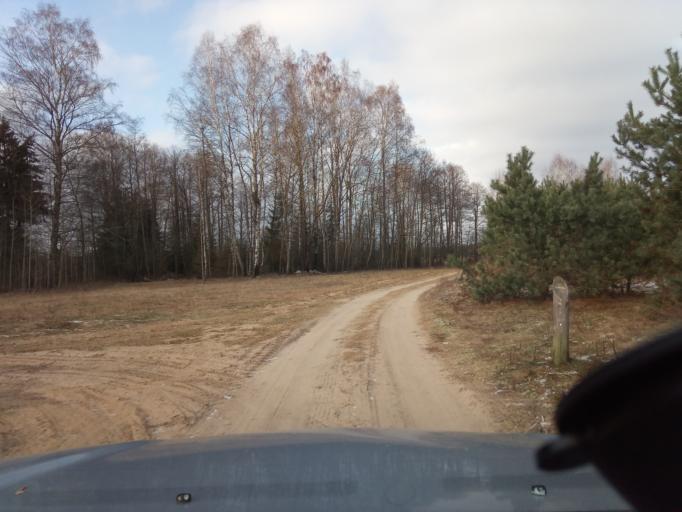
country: LT
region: Alytaus apskritis
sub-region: Alytaus rajonas
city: Daugai
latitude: 54.1110
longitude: 24.2402
